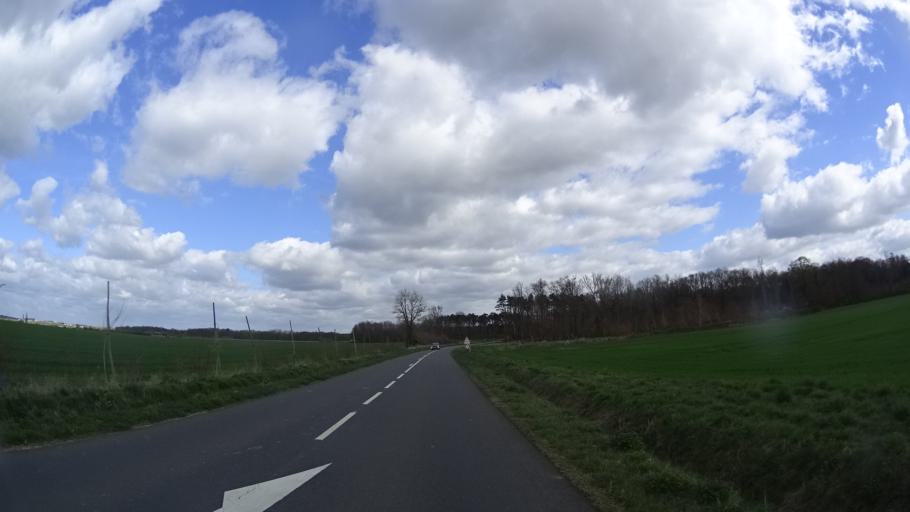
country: FR
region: Pays de la Loire
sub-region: Departement de Maine-et-Loire
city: Breze
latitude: 47.0846
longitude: -0.0117
